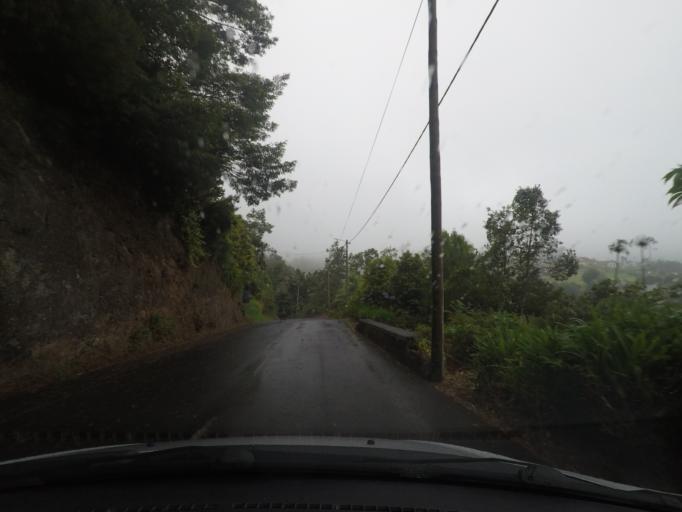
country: PT
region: Madeira
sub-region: Santana
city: Santana
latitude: 32.7951
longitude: -16.8665
